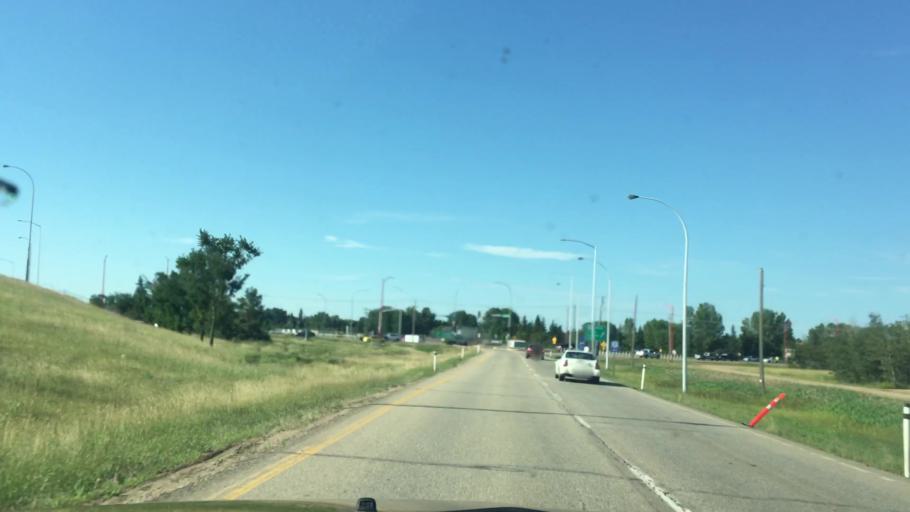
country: CA
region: Alberta
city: Leduc
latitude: 53.2664
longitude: -113.5643
